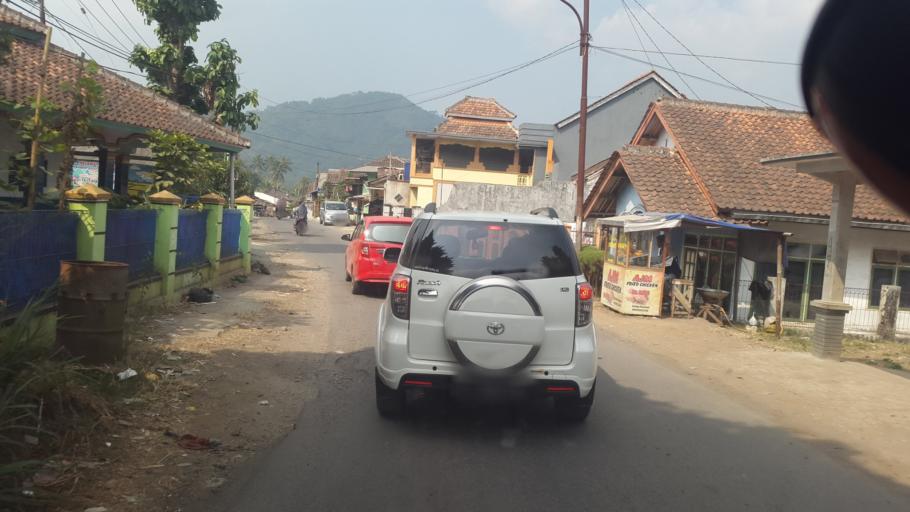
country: ID
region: West Java
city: Sukabumi
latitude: -6.9317
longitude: 106.9814
